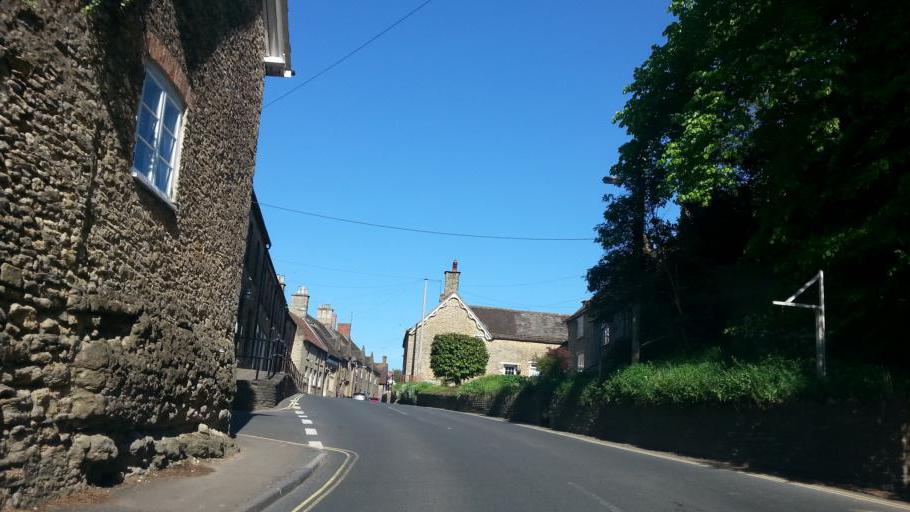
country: GB
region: England
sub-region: Somerset
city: Milborne Port
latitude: 50.9661
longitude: -2.4631
